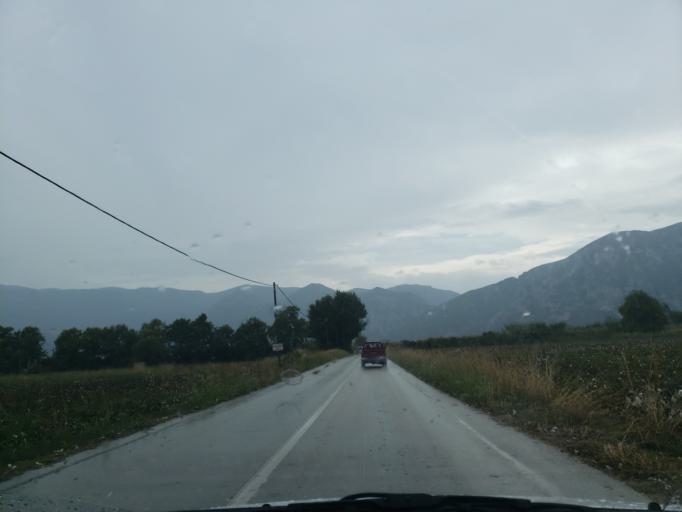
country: GR
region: Central Greece
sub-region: Nomos Fthiotidos
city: Anthili
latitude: 38.8196
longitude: 22.4420
